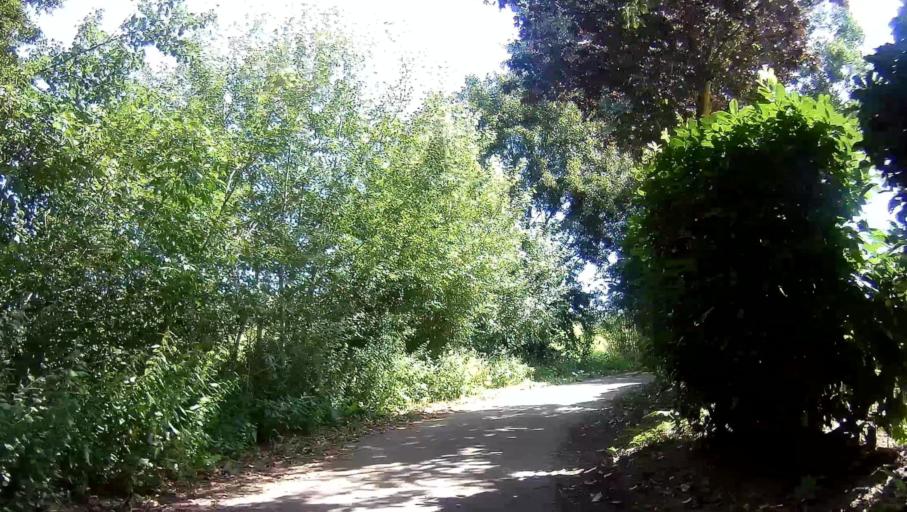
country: NL
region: South Holland
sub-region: Gemeente Ridderkerk
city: Ridderkerk
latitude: 51.8712
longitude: 4.6267
